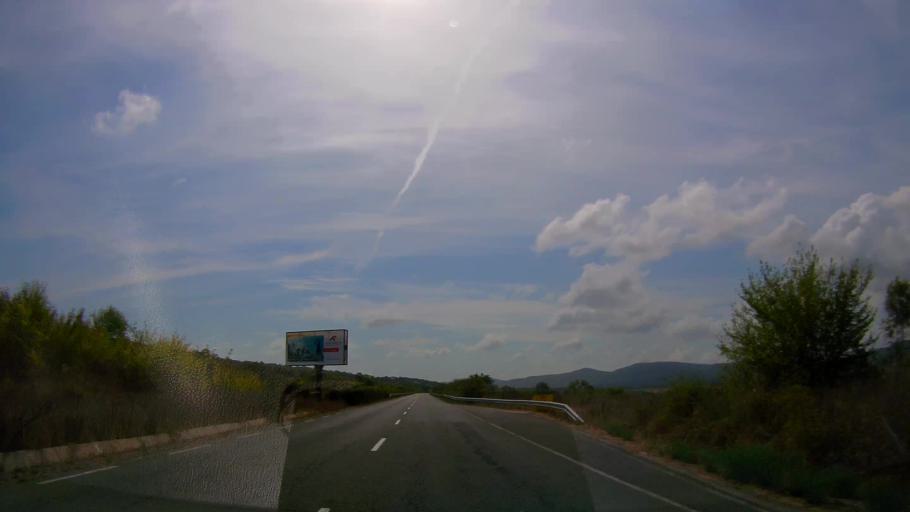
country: BG
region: Burgas
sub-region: Obshtina Sozopol
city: Sozopol
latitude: 42.3861
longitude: 27.6794
